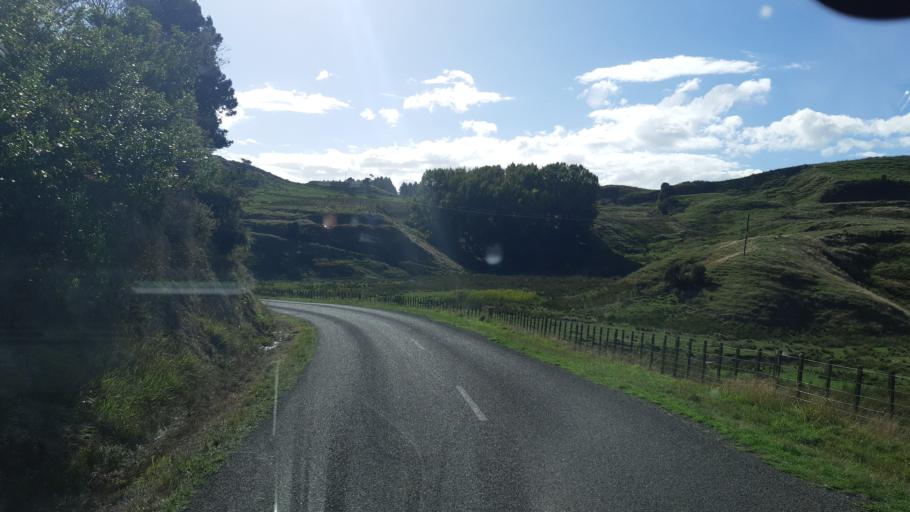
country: NZ
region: Manawatu-Wanganui
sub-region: Rangitikei District
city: Bulls
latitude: -39.9014
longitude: 175.3400
